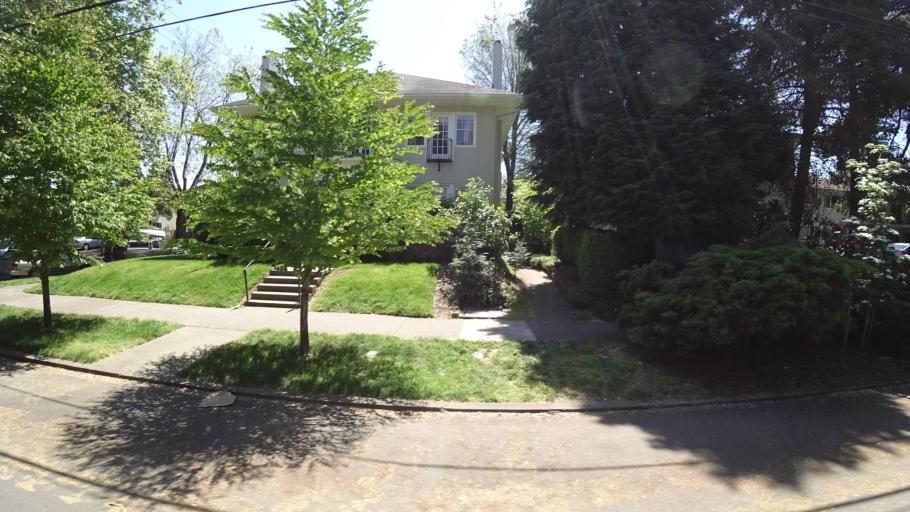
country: US
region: Oregon
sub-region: Multnomah County
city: Portland
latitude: 45.5364
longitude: -122.6469
